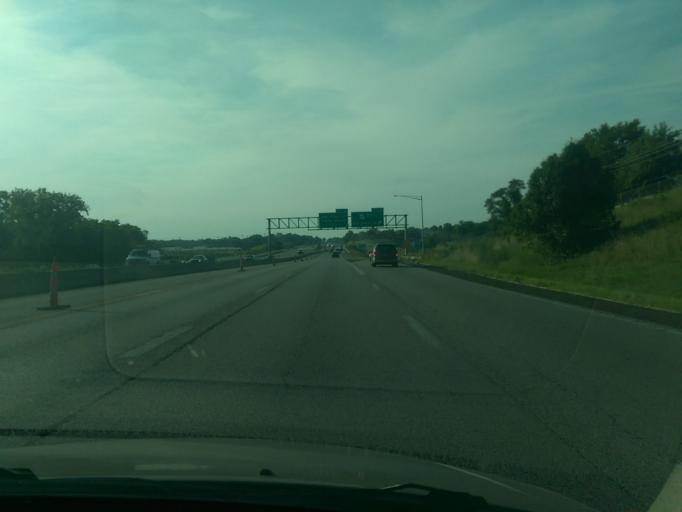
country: US
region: Missouri
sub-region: Platte County
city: Riverside
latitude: 39.2074
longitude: -94.6357
